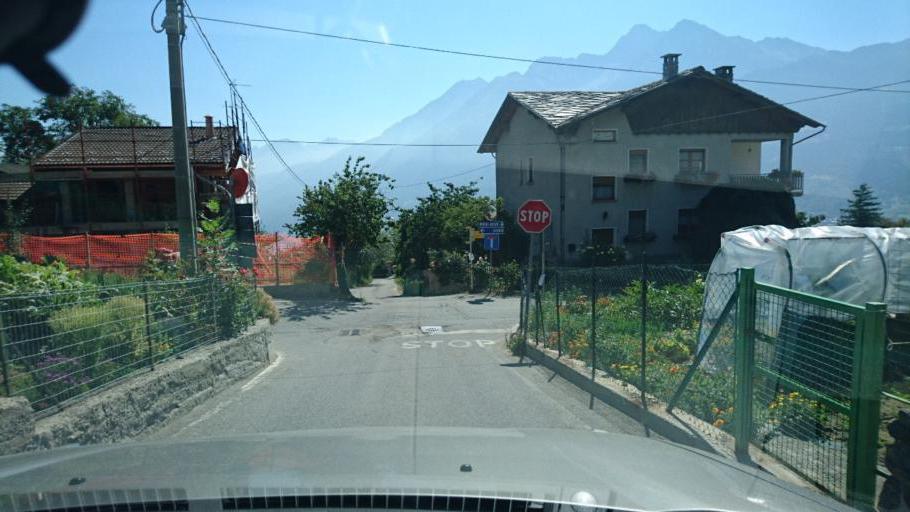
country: IT
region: Aosta Valley
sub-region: Valle d'Aosta
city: Aosta
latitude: 45.7504
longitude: 7.3056
